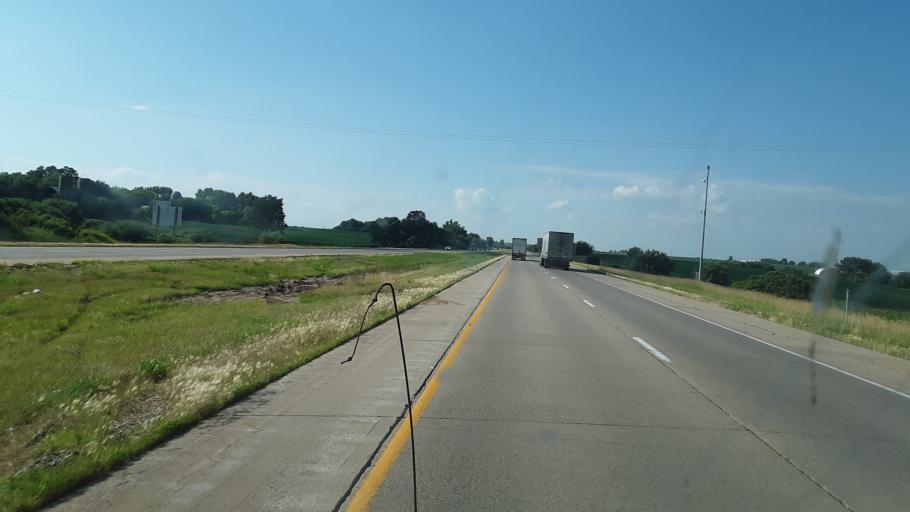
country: US
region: Iowa
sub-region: Black Hawk County
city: Elk Run Heights
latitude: 42.4273
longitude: -92.1864
